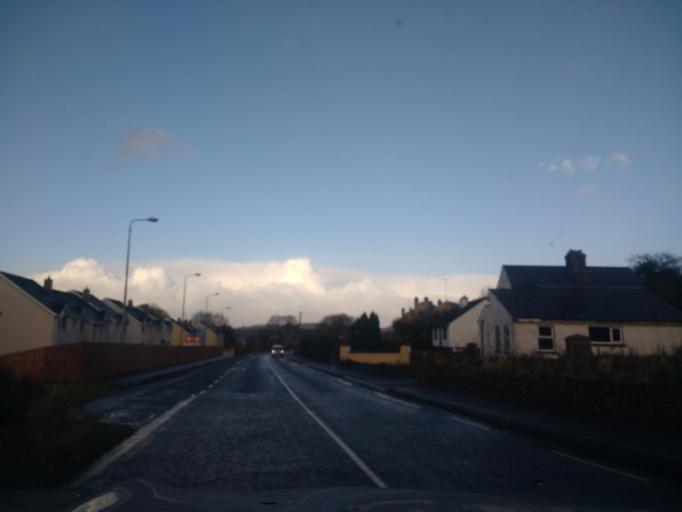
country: IE
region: Ulster
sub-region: County Donegal
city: Ramelton
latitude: 55.0320
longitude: -7.6505
